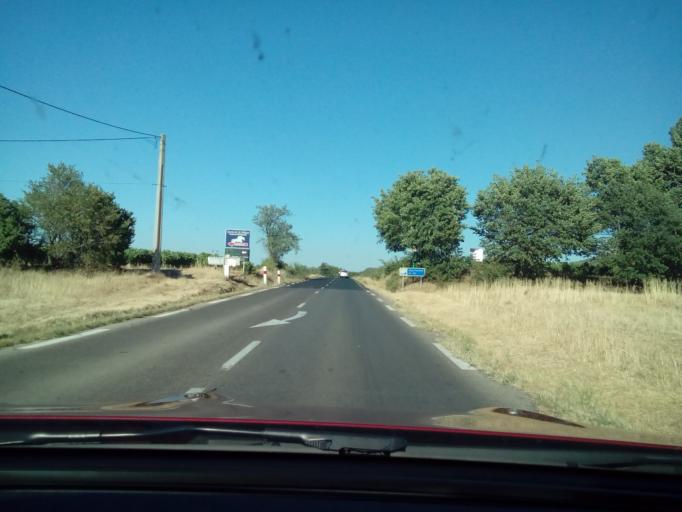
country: FR
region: Provence-Alpes-Cote d'Azur
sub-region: Departement du Var
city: Pourrieres
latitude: 43.4654
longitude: 5.7284
